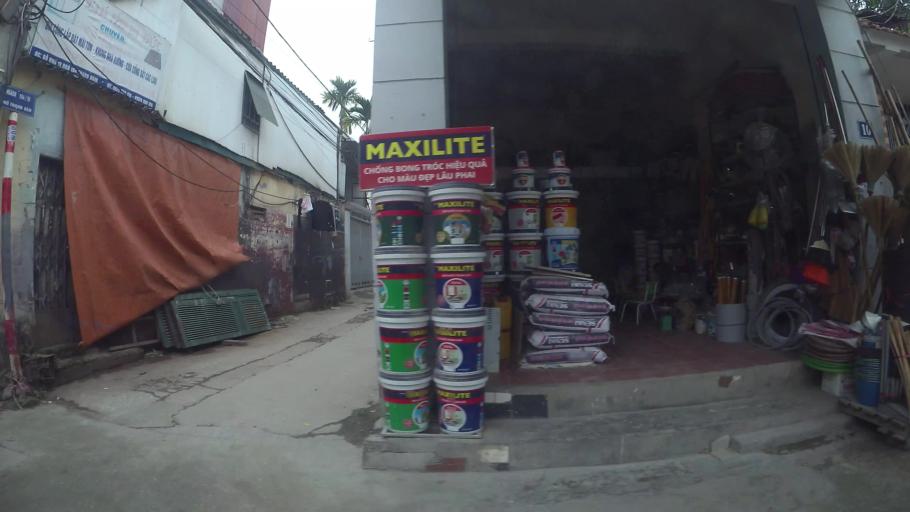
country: VN
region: Ha Noi
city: Hai BaTrung
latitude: 20.9956
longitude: 105.8859
